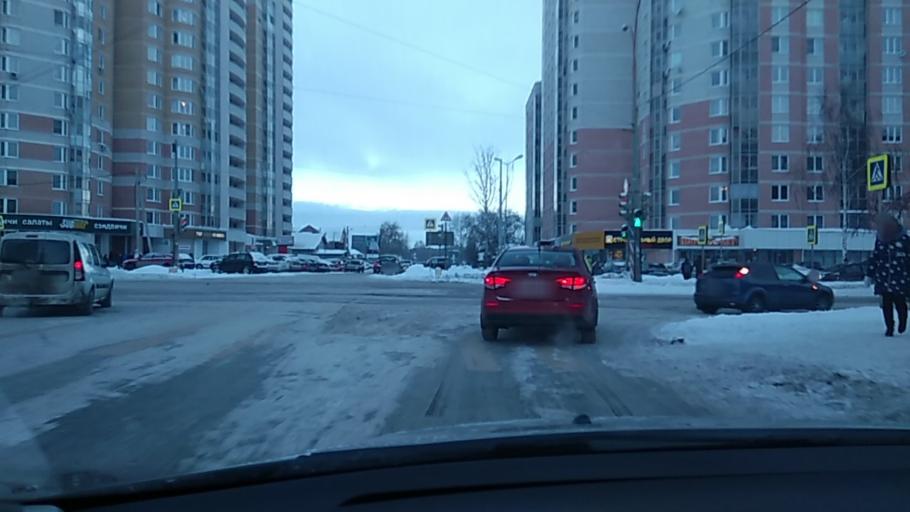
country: RU
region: Sverdlovsk
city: Yekaterinburg
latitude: 56.9039
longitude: 60.5865
